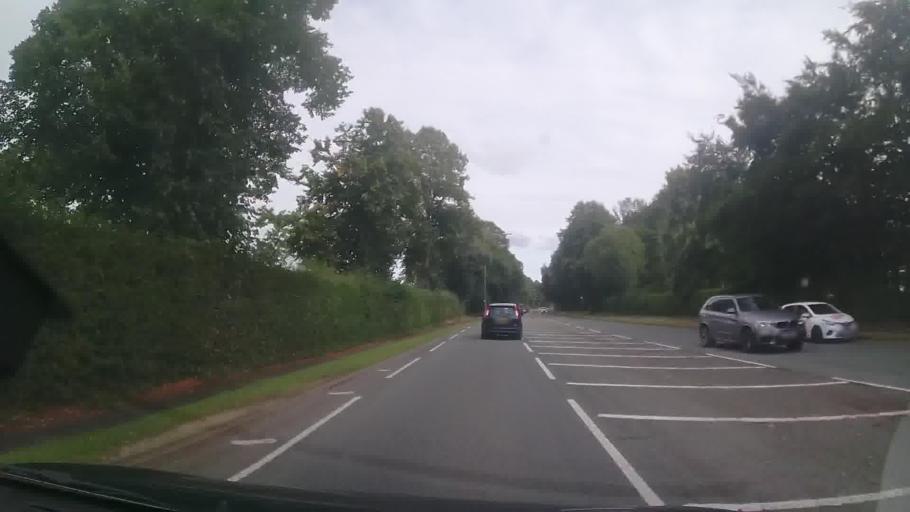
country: GB
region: England
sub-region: Shropshire
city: Bicton
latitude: 52.7128
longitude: -2.7877
